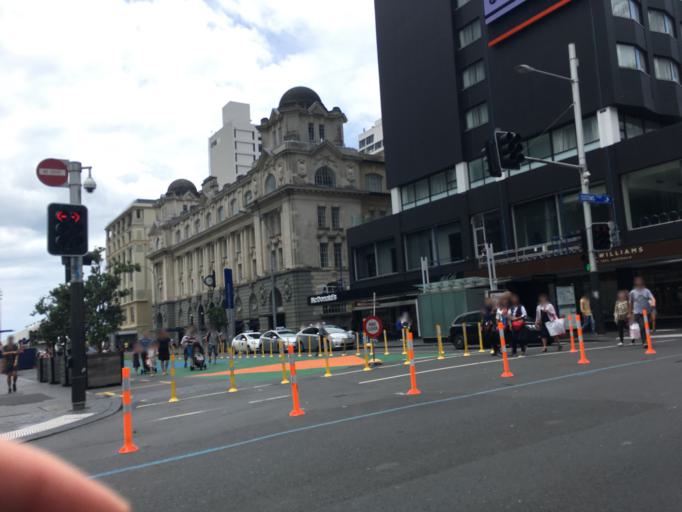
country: NZ
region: Auckland
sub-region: Auckland
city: Auckland
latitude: -36.8446
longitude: 174.7665
